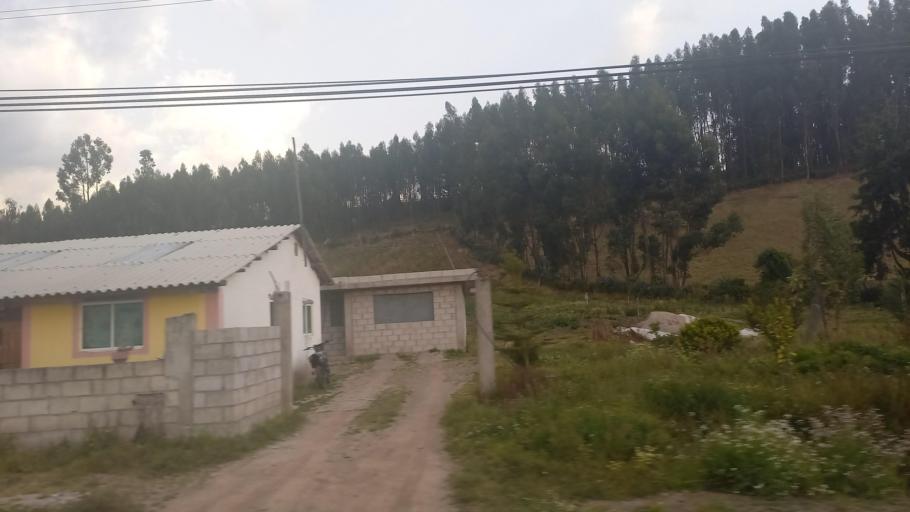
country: EC
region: Pichincha
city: Cayambe
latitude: 0.0848
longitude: -78.1033
